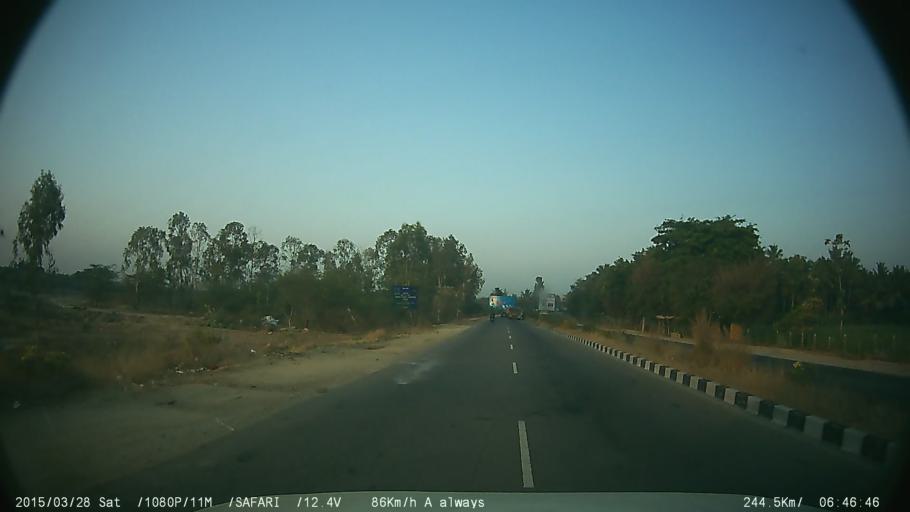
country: IN
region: Karnataka
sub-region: Mandya
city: Maddur
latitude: 12.6150
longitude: 77.0834
